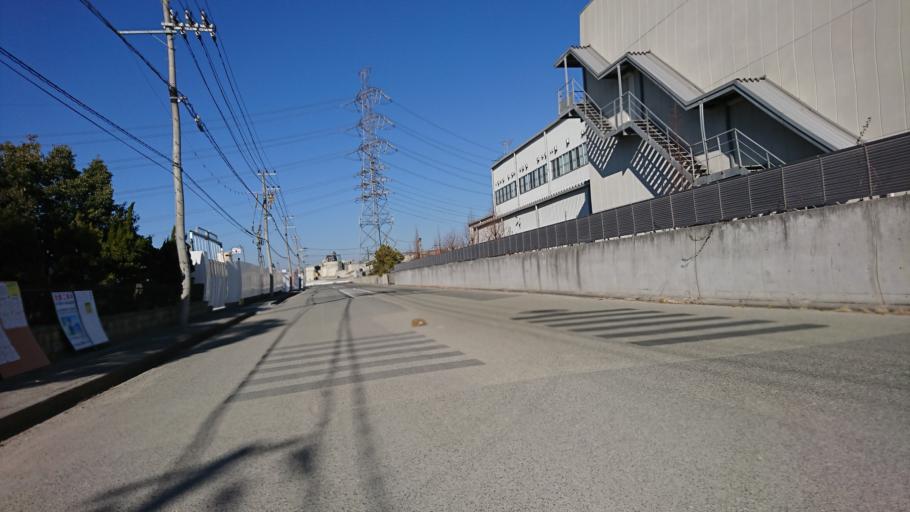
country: JP
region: Hyogo
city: Shirahamacho-usazakiminami
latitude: 34.7585
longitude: 134.7683
